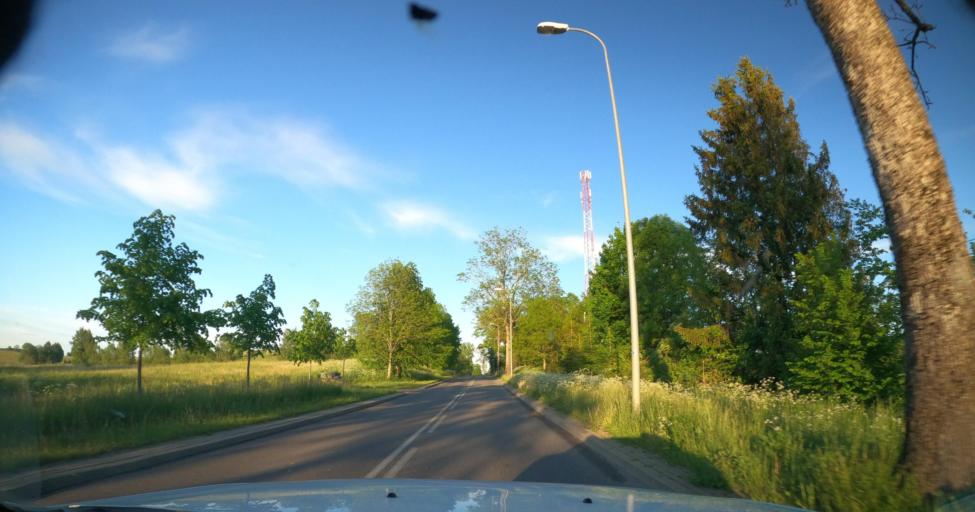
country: PL
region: Warmian-Masurian Voivodeship
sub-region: Powiat lidzbarski
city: Lidzbark Warminski
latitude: 54.1461
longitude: 20.4784
